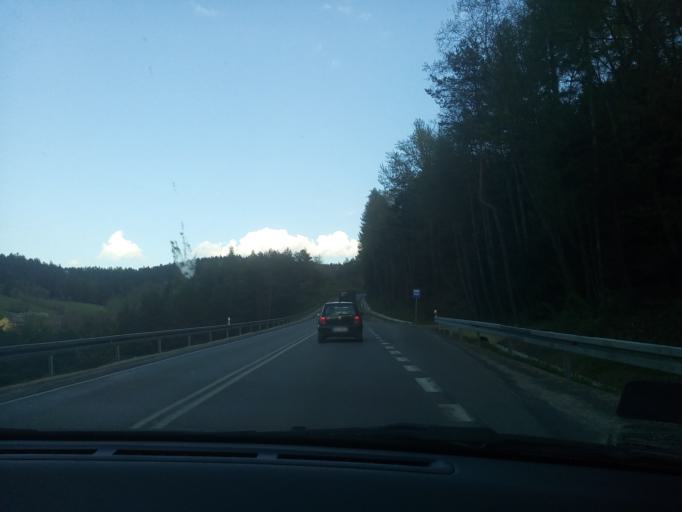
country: PL
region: Lesser Poland Voivodeship
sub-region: Powiat nowosadecki
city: Krynica-Zdroj
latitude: 49.4742
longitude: 20.9411
